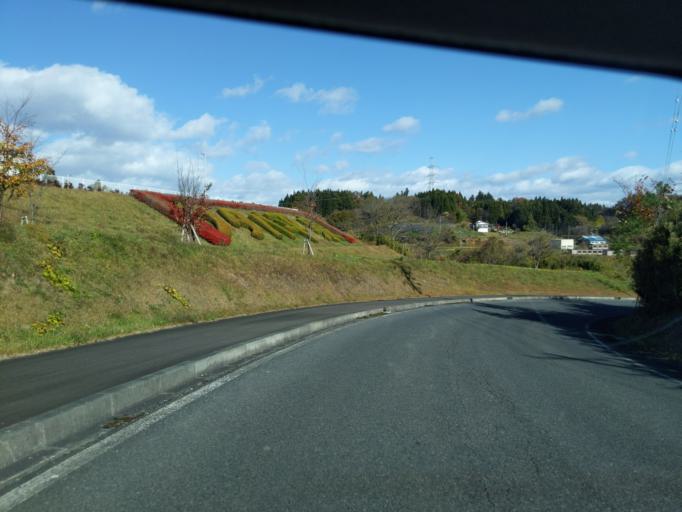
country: JP
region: Iwate
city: Ichinoseki
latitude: 39.0221
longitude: 141.1094
